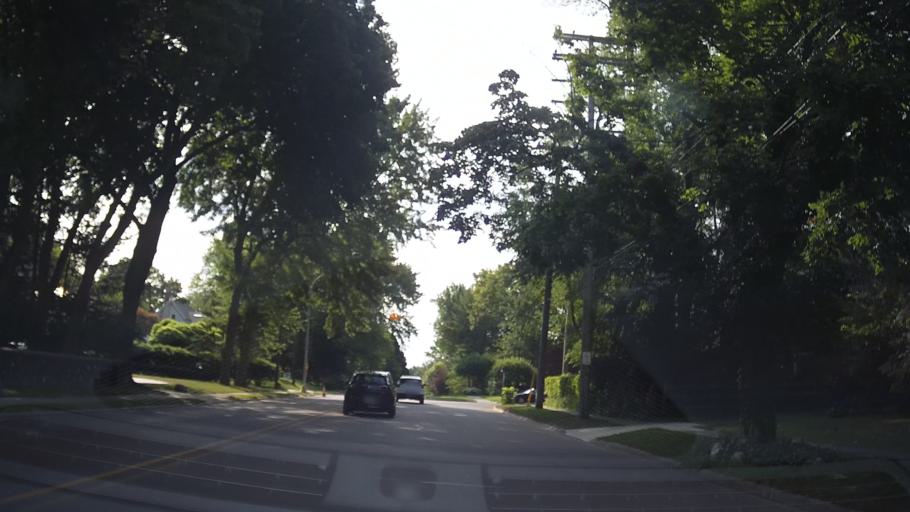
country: US
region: Michigan
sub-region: Wayne County
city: Grosse Pointe Farms
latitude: 42.4088
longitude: -82.8904
